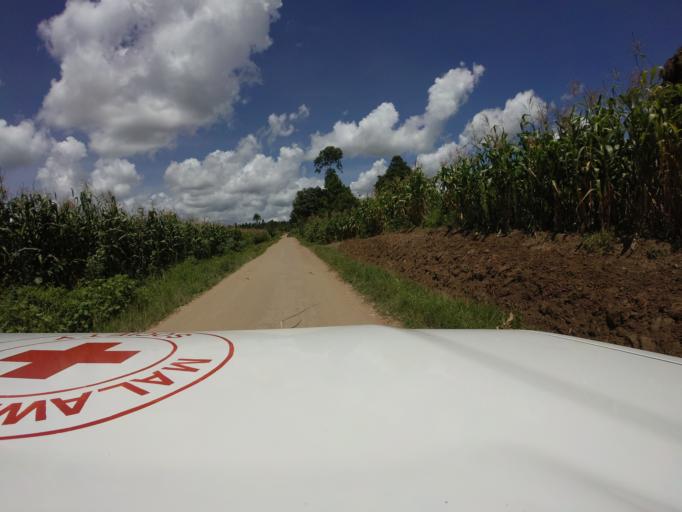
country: MW
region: Southern Region
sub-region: Thyolo District
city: Thyolo
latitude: -15.9542
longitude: 35.1589
